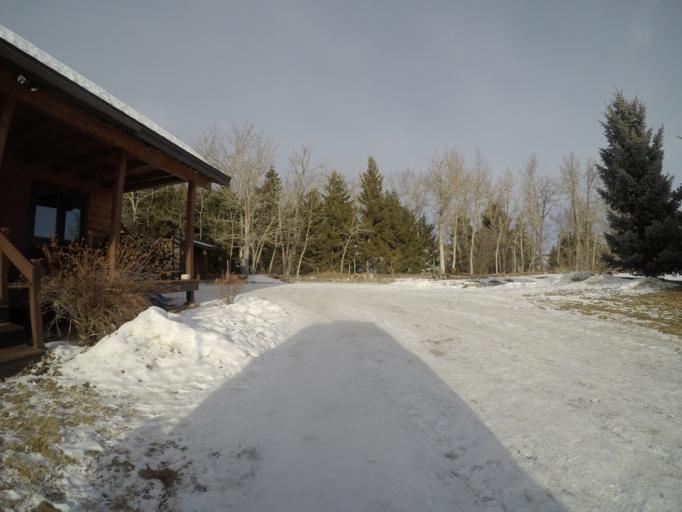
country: US
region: Montana
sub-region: Carbon County
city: Red Lodge
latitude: 45.1593
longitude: -109.2995
